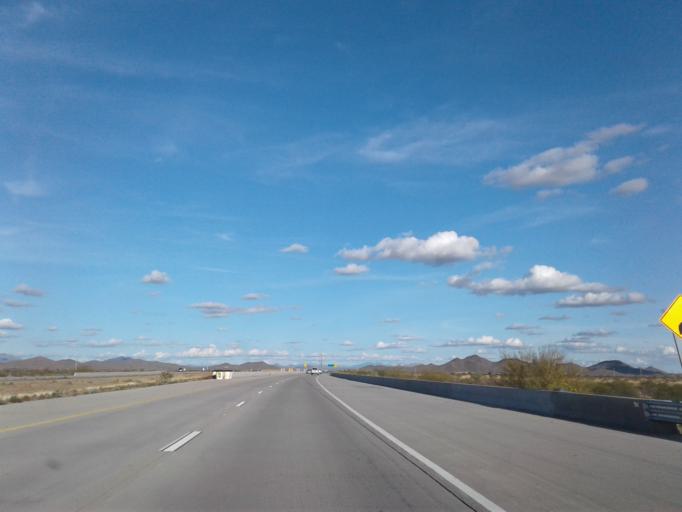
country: US
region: Arizona
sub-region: Maricopa County
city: Anthem
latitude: 33.7680
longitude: -112.1596
